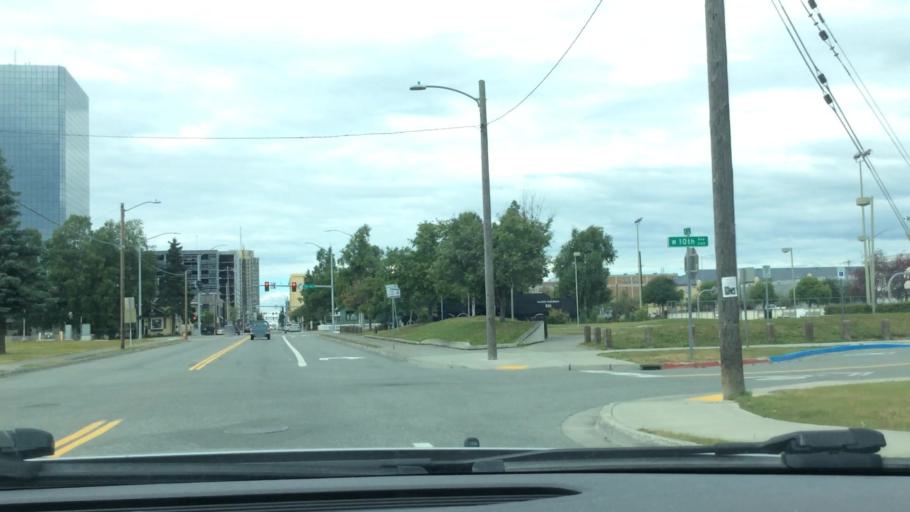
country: US
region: Alaska
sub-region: Anchorage Municipality
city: Anchorage
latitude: 61.2126
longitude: -149.8914
